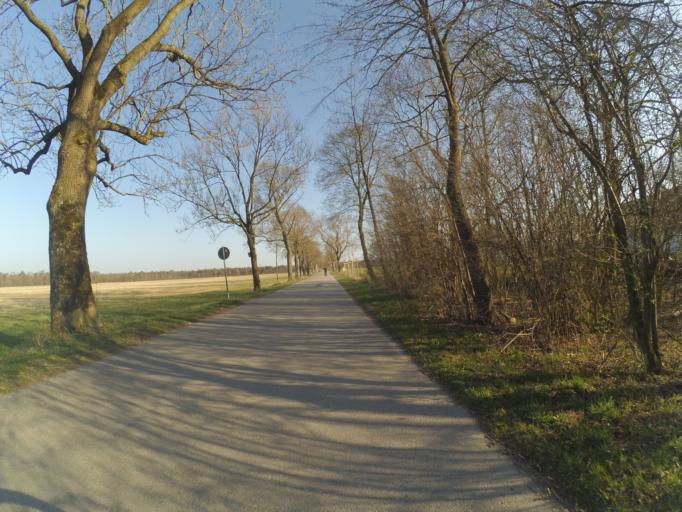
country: DE
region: Bavaria
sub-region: Upper Bavaria
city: Oberschleissheim
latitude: 48.2361
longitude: 11.5771
